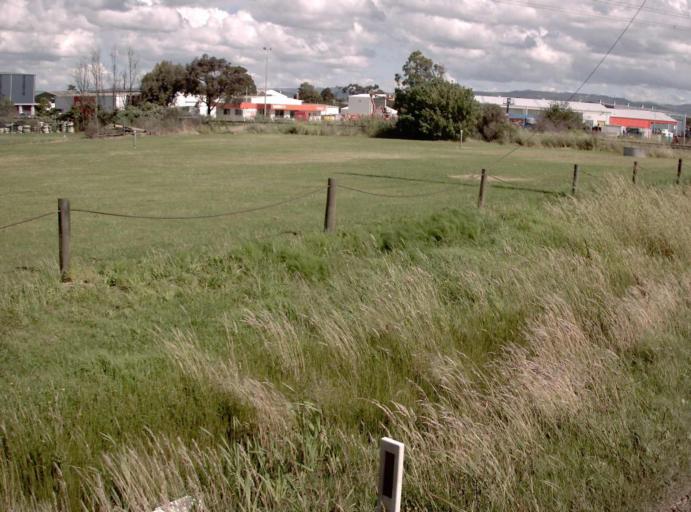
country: AU
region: Victoria
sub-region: Latrobe
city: Morwell
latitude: -38.2350
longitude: 146.4384
